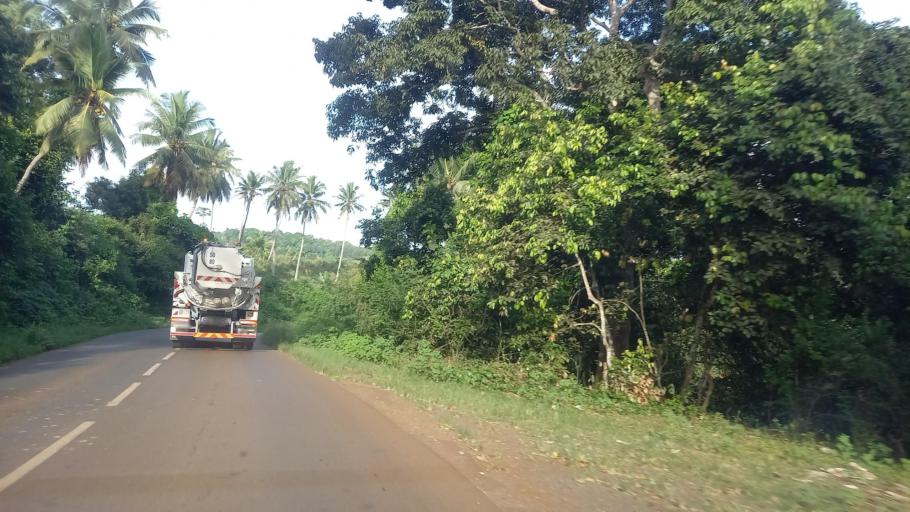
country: YT
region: Chiconi
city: Chiconi
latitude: -12.8205
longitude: 45.1297
